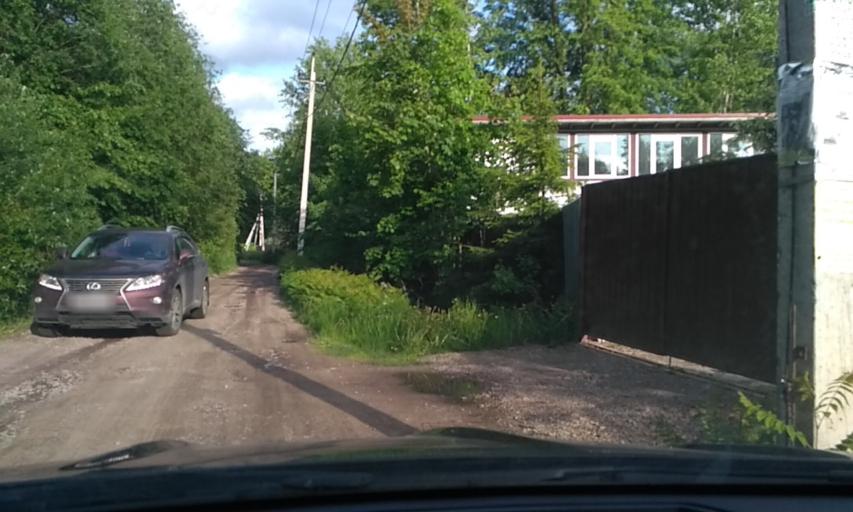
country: RU
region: Leningrad
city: Otradnoye
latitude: 59.8067
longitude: 30.8133
